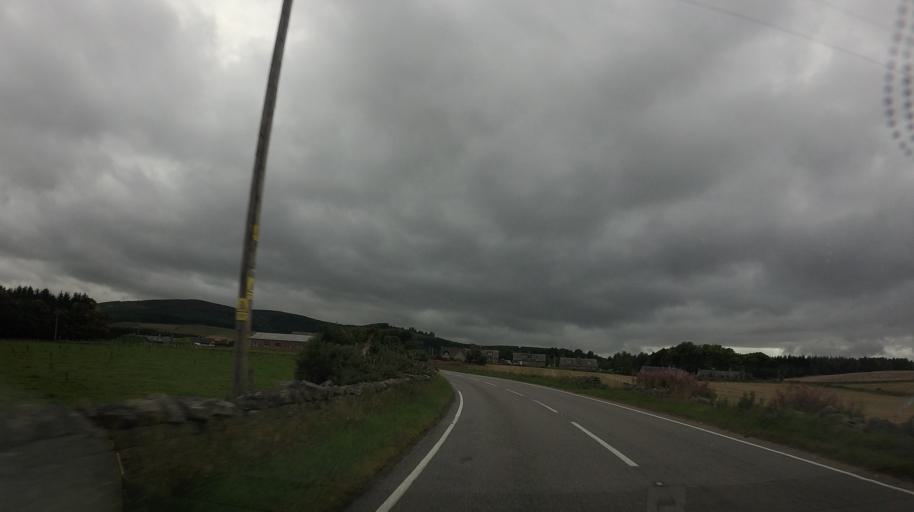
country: GB
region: Scotland
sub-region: Aberdeenshire
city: Torphins
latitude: 57.1873
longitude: -2.5583
